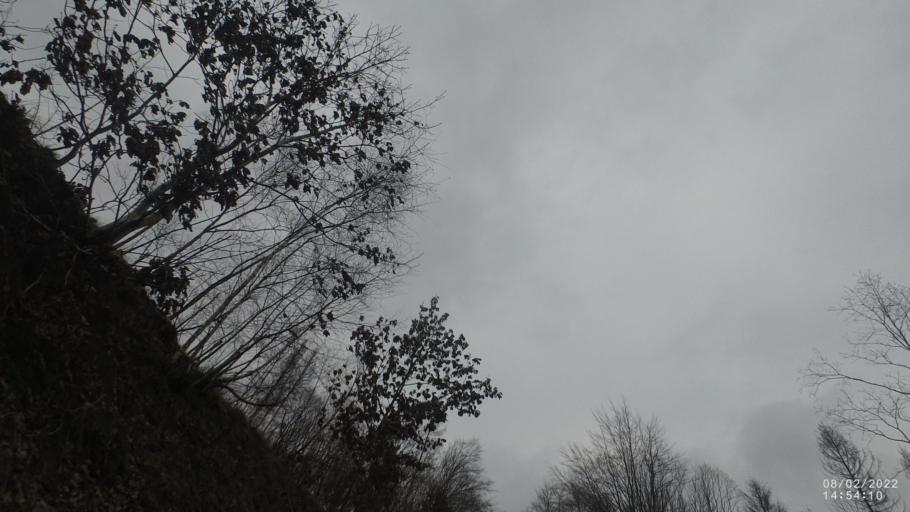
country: DE
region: North Rhine-Westphalia
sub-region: Regierungsbezirk Arnsberg
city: Schalksmuhle
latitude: 51.2547
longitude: 7.5642
